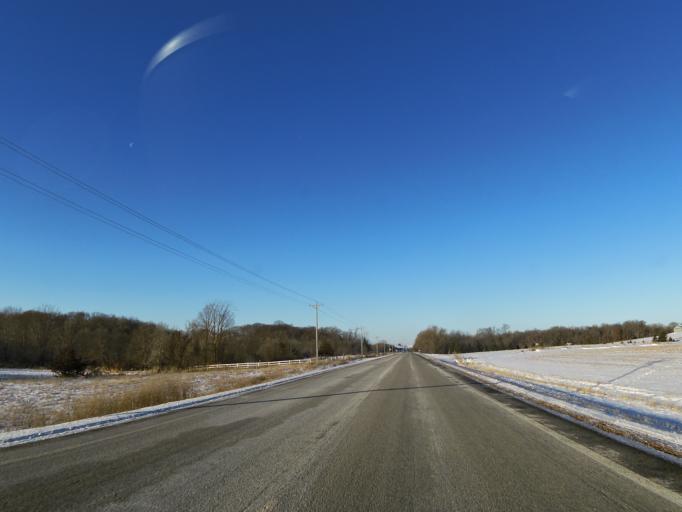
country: US
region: Minnesota
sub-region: Le Sueur County
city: New Prague
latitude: 44.6304
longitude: -93.5257
